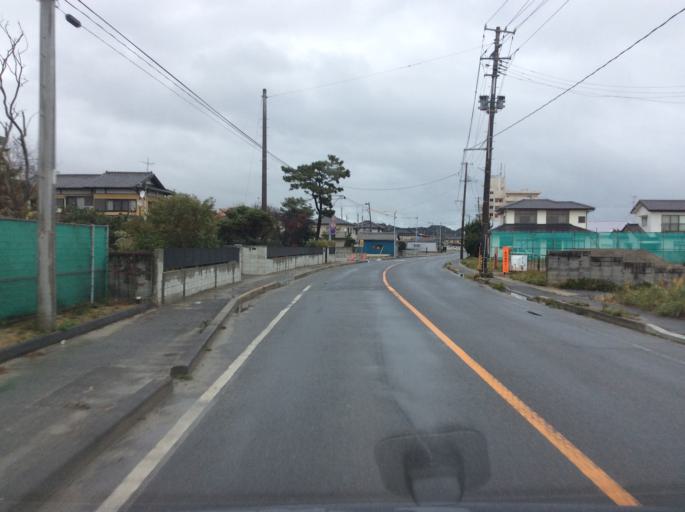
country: JP
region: Fukushima
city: Iwaki
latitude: 37.0990
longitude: 140.9859
